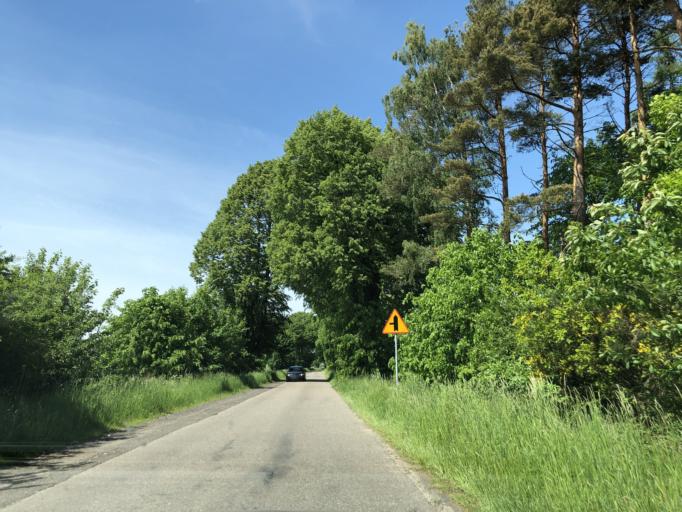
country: PL
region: West Pomeranian Voivodeship
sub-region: Powiat kolobrzeski
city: Dygowo
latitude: 54.0995
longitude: 15.7085
